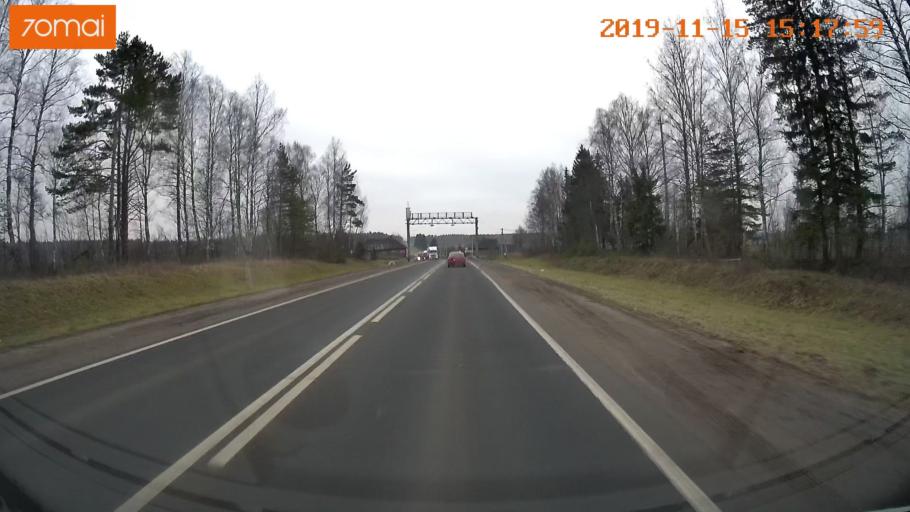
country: RU
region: Jaroslavl
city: Danilov
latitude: 58.2532
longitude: 40.1806
